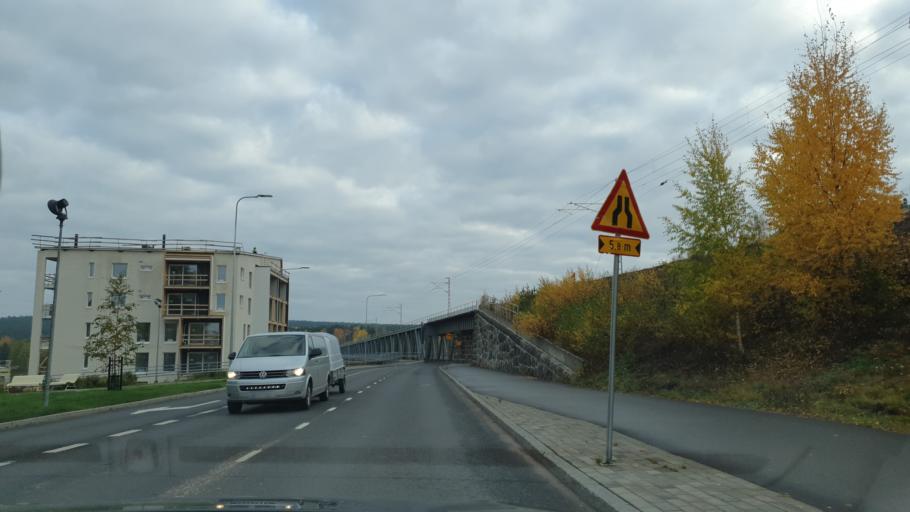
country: FI
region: Lapland
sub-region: Rovaniemi
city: Rovaniemi
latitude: 66.4957
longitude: 25.7314
